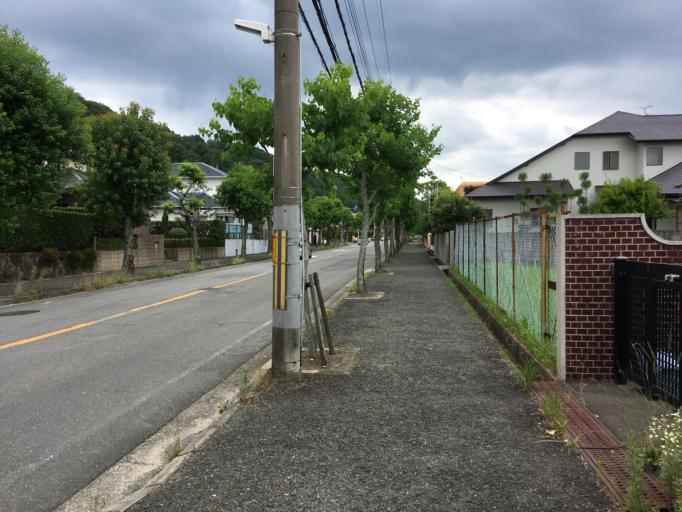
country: JP
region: Nara
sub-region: Ikoma-shi
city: Ikoma
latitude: 34.6805
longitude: 135.7176
